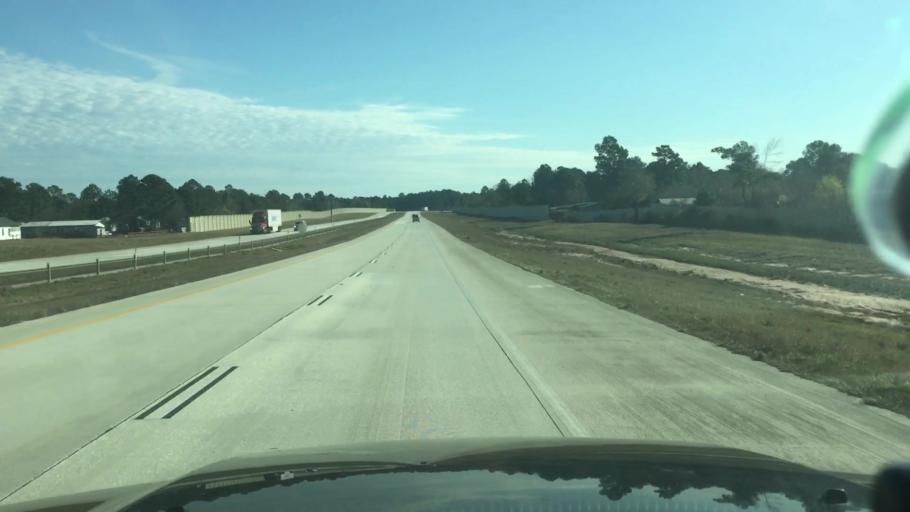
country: US
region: Texas
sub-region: Montgomery County
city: Porter Heights
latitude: 30.1377
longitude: -95.2687
